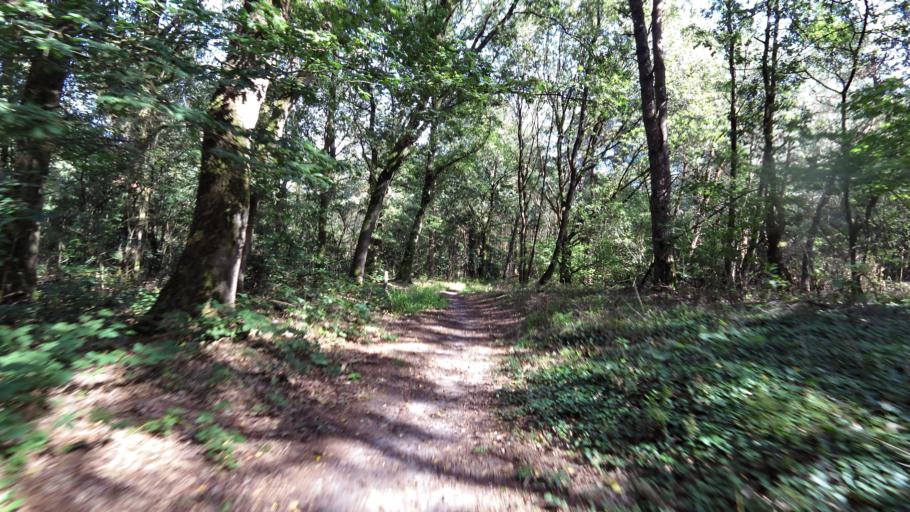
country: NL
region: Gelderland
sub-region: Gemeente Ede
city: Bennekom
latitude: 52.0141
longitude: 5.7079
